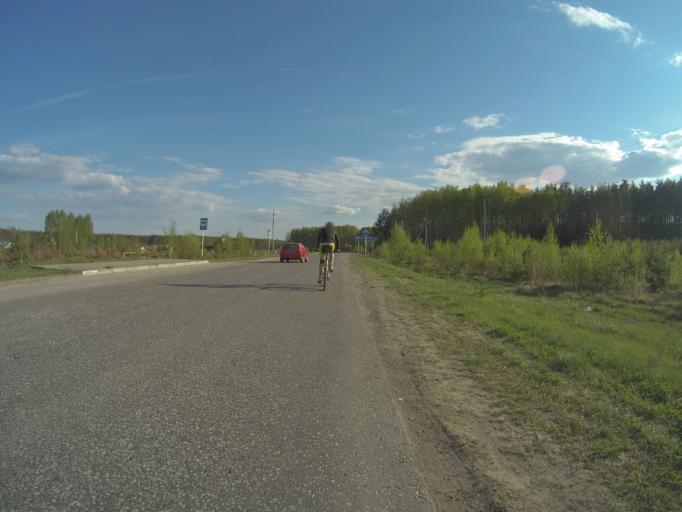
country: RU
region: Vladimir
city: Sudogda
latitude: 56.0897
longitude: 40.7857
